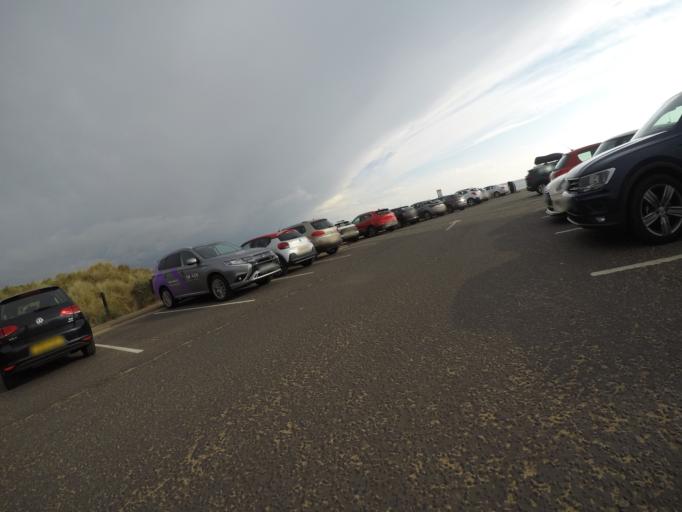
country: GB
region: Scotland
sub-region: North Ayrshire
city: Irvine
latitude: 55.6049
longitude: -4.6941
